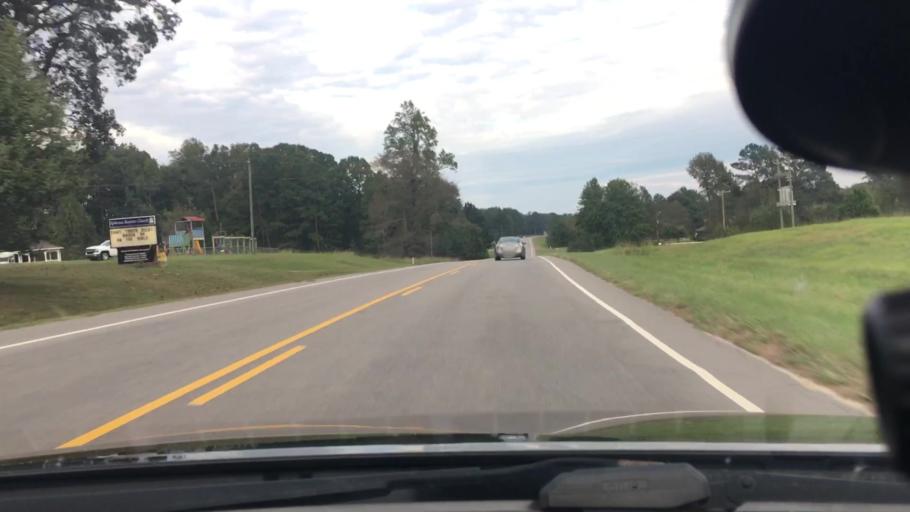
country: US
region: North Carolina
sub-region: Lee County
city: Sanford
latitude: 35.3877
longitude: -79.2709
